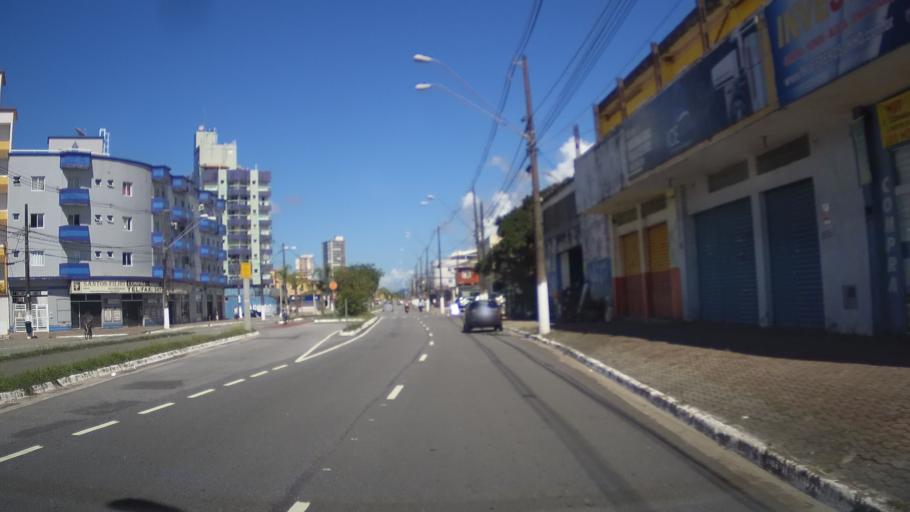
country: BR
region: Sao Paulo
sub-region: Mongagua
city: Mongagua
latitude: -24.0429
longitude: -46.5210
